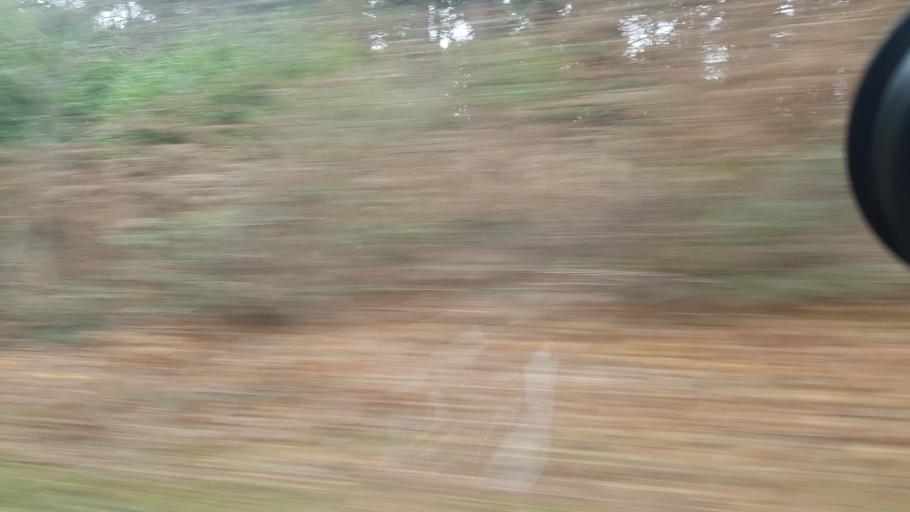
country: GB
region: England
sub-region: Hampshire
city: Yateley
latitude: 51.3143
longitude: -0.8158
